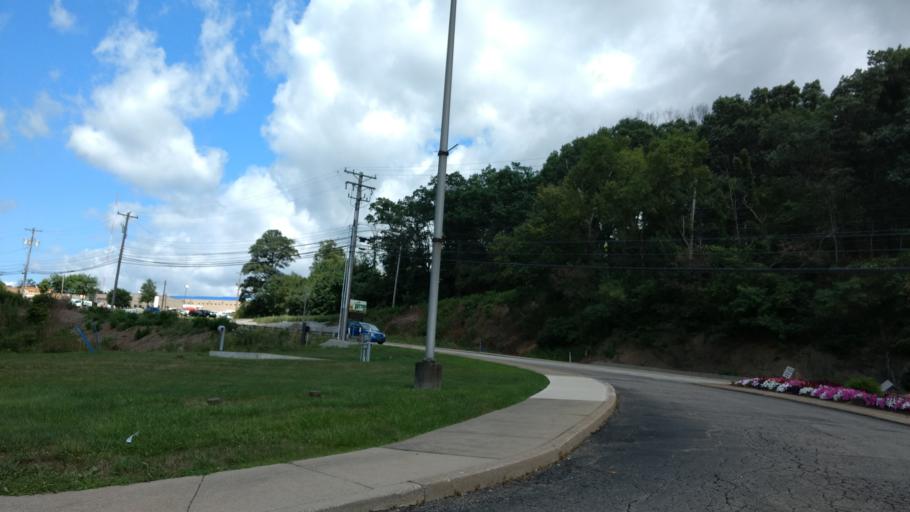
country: US
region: Pennsylvania
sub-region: Westmoreland County
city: Murrysville
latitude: 40.4289
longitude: -79.7080
